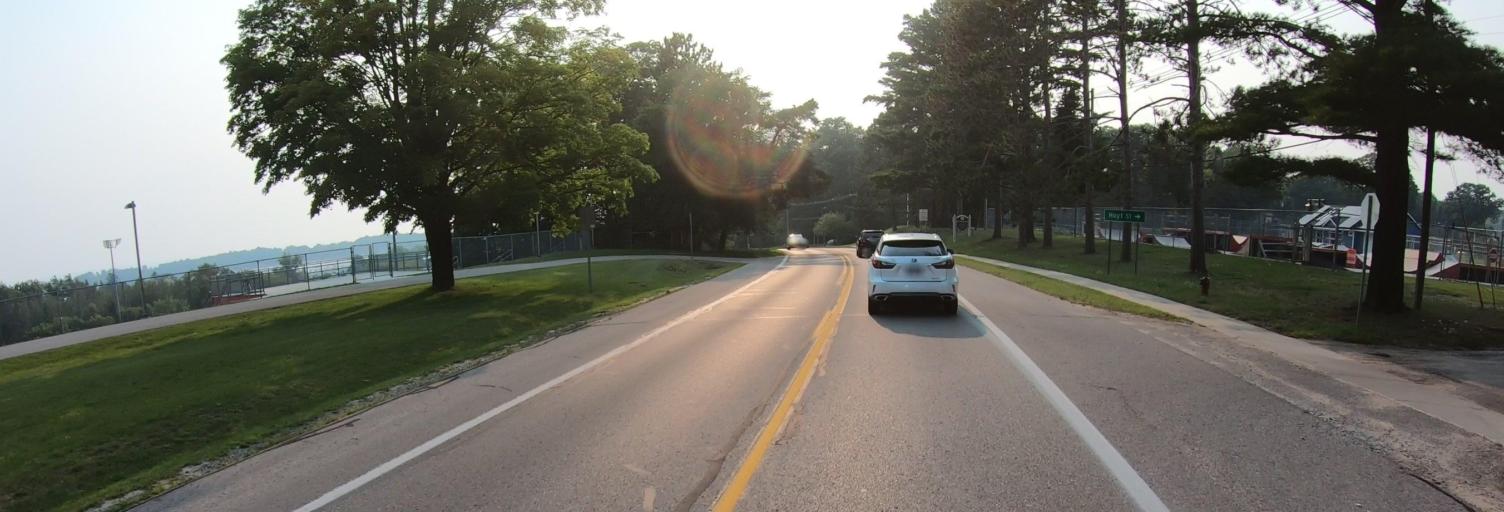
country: US
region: Michigan
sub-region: Emmet County
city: Harbor Springs
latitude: 45.4328
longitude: -84.9731
